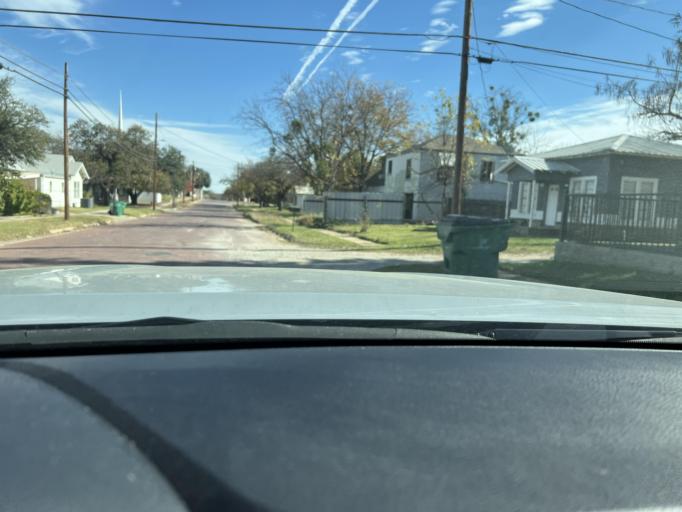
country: US
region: Texas
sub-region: Eastland County
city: Eastland
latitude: 32.3995
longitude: -98.8238
